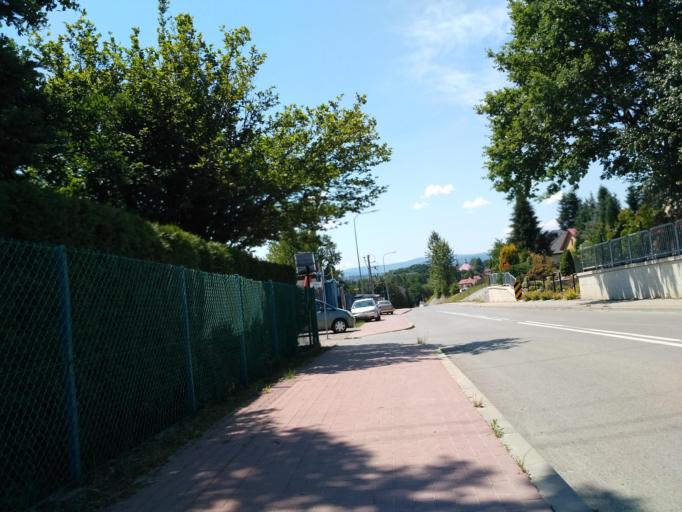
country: PL
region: Subcarpathian Voivodeship
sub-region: Krosno
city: Krosno
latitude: 49.7059
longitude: 21.7804
